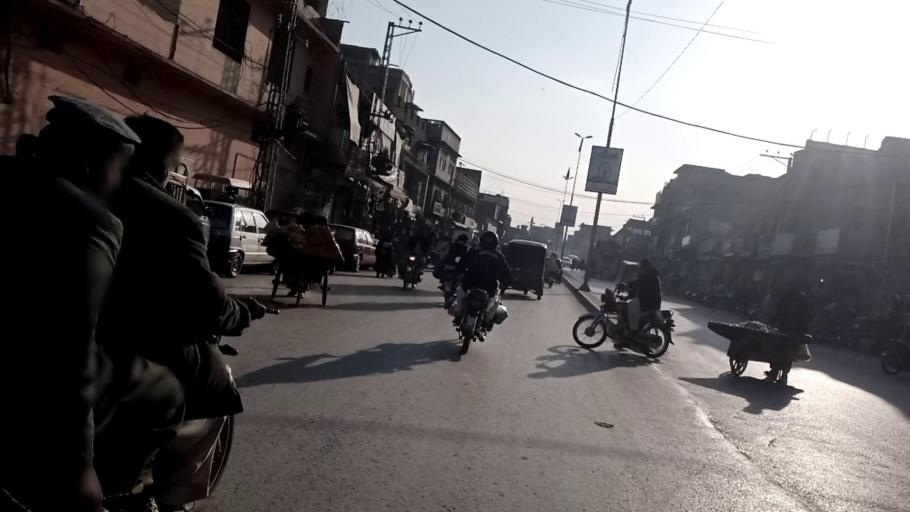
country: PK
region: Khyber Pakhtunkhwa
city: Peshawar
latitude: 34.0014
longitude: 71.5678
